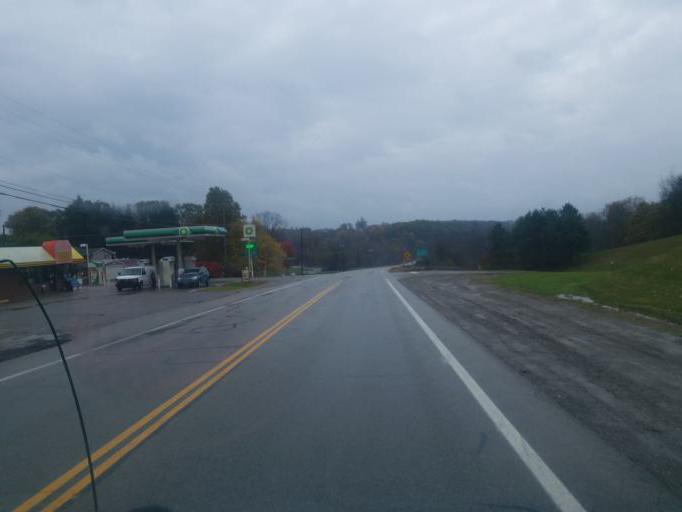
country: US
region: Ohio
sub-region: Muskingum County
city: Frazeysburg
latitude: 40.0266
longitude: -82.0985
